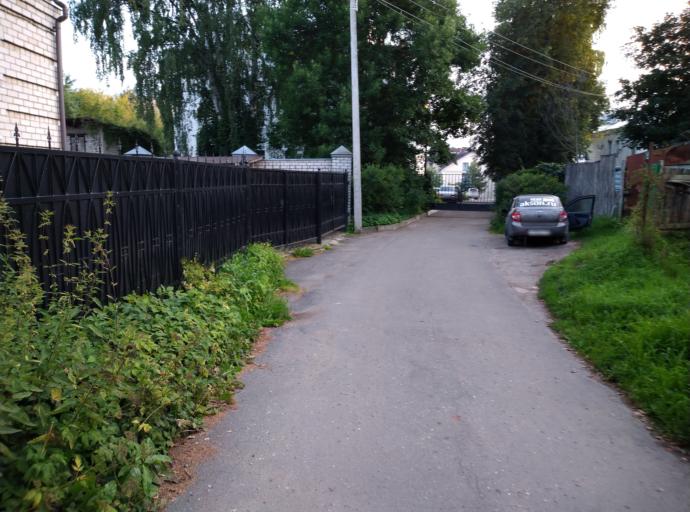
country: RU
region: Kostroma
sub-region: Kostromskoy Rayon
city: Kostroma
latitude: 57.7630
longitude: 40.9368
